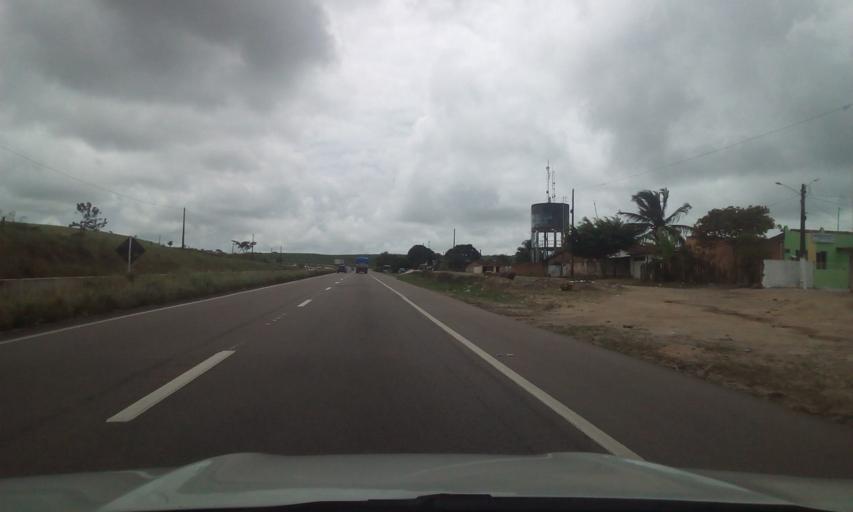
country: BR
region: Pernambuco
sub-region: Itapissuma
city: Itapissuma
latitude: -7.7475
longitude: -34.9371
